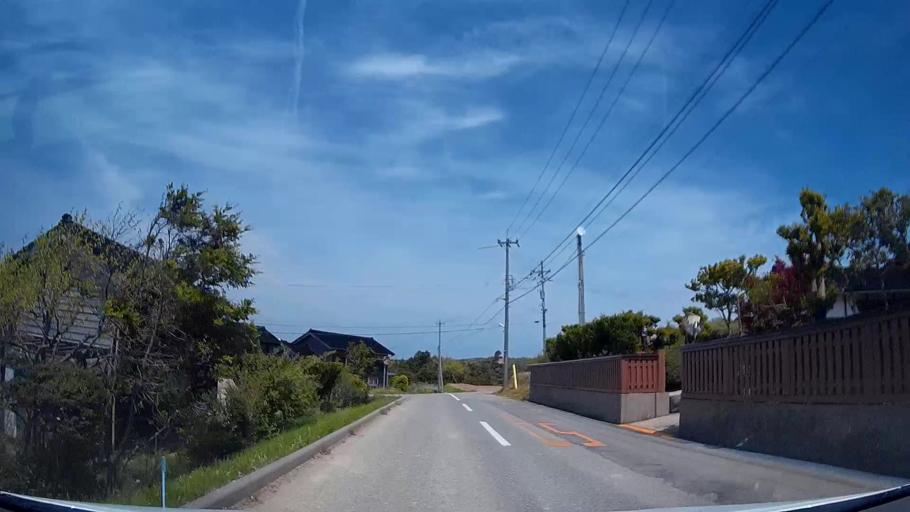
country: JP
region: Ishikawa
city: Hakui
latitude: 36.9503
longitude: 136.7777
